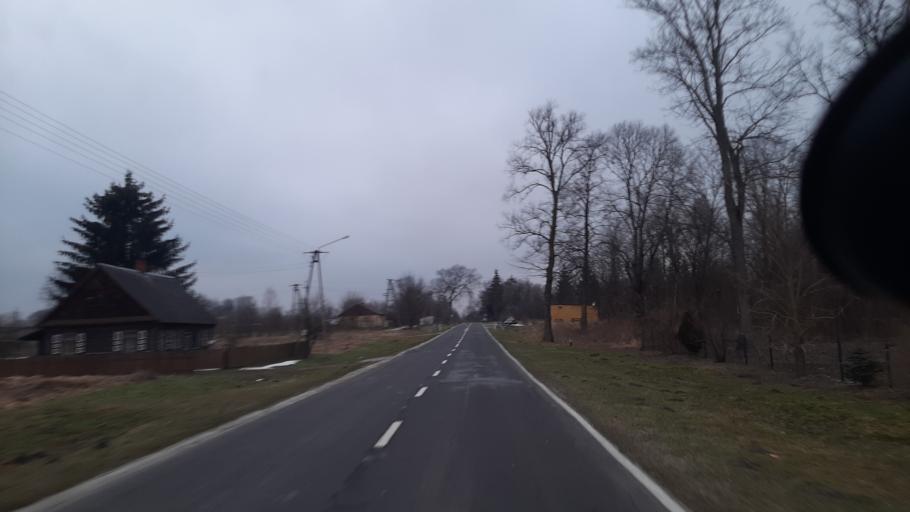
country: PL
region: Lublin Voivodeship
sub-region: Powiat parczewski
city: Podedworze
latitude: 51.5893
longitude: 23.2007
